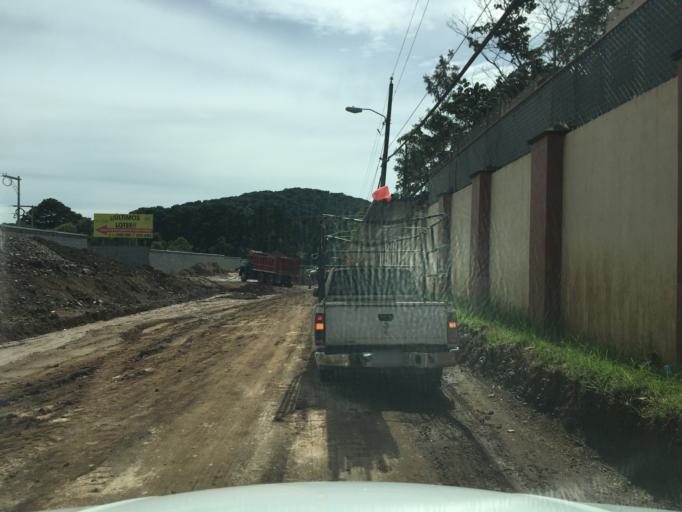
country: GT
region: Guatemala
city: Mixco
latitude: 14.6531
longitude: -90.5650
